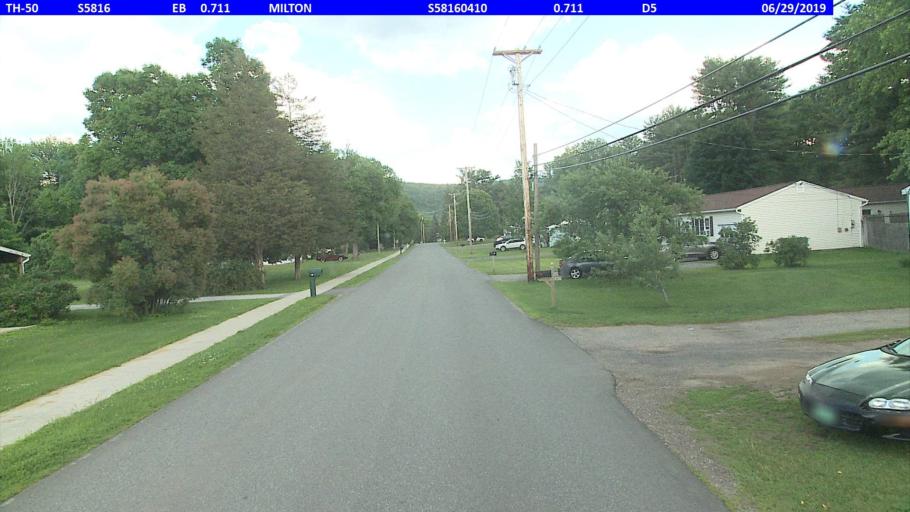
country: US
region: Vermont
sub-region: Chittenden County
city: Milton
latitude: 44.6159
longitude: -73.1140
